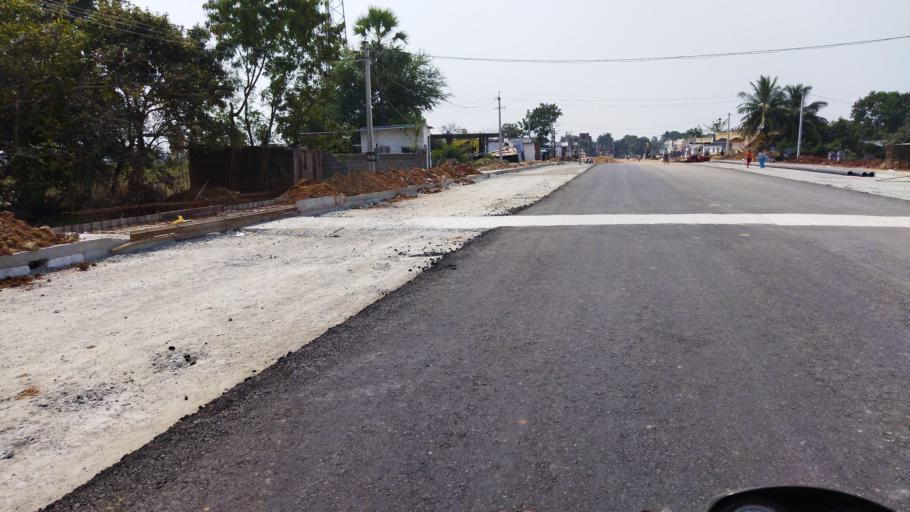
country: IN
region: Telangana
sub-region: Nalgonda
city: Nalgonda
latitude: 17.1445
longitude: 79.3947
